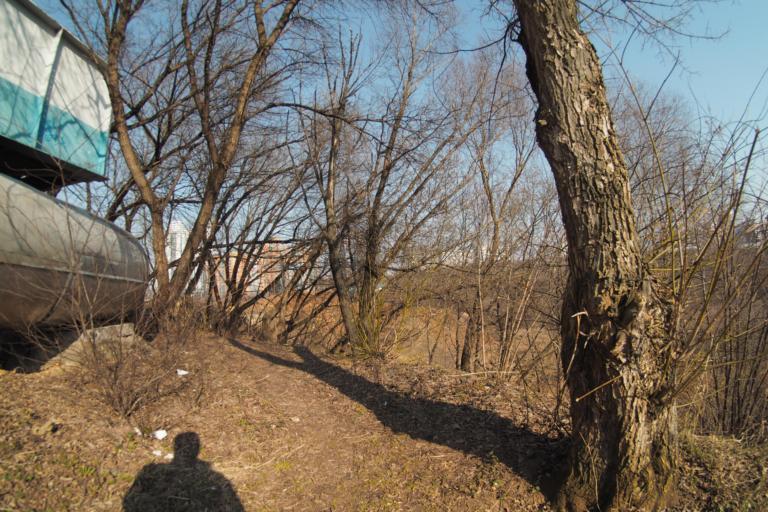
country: RU
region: Moskovskaya
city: Kastanayevo
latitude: 55.7110
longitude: 37.4921
